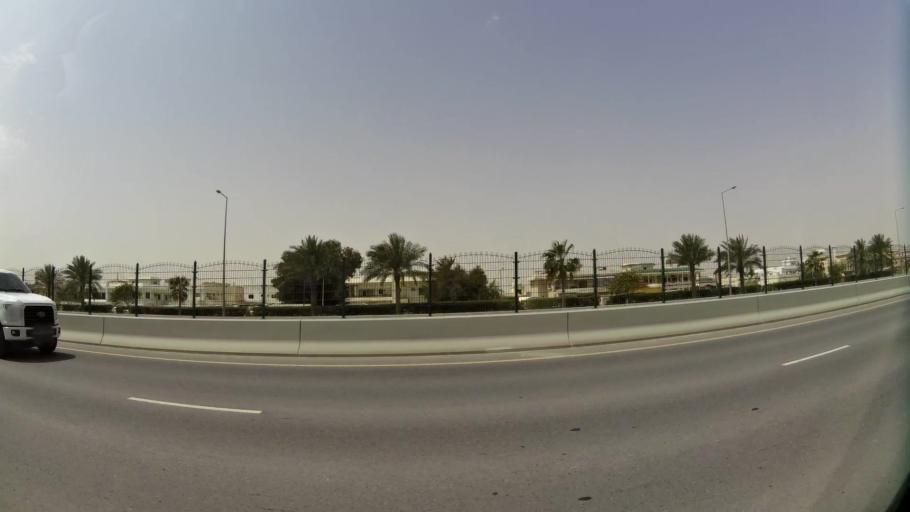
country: QA
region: Baladiyat ar Rayyan
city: Ar Rayyan
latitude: 25.2317
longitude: 51.4313
